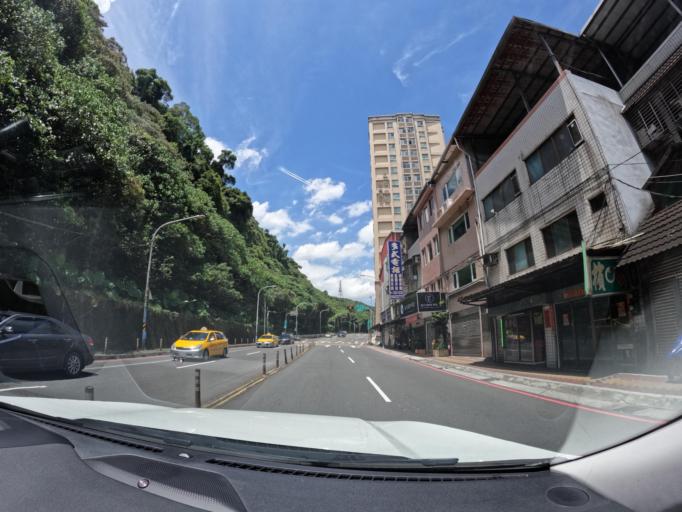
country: TW
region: Taipei
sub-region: Taipei
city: Banqiao
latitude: 25.0277
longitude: 121.4106
